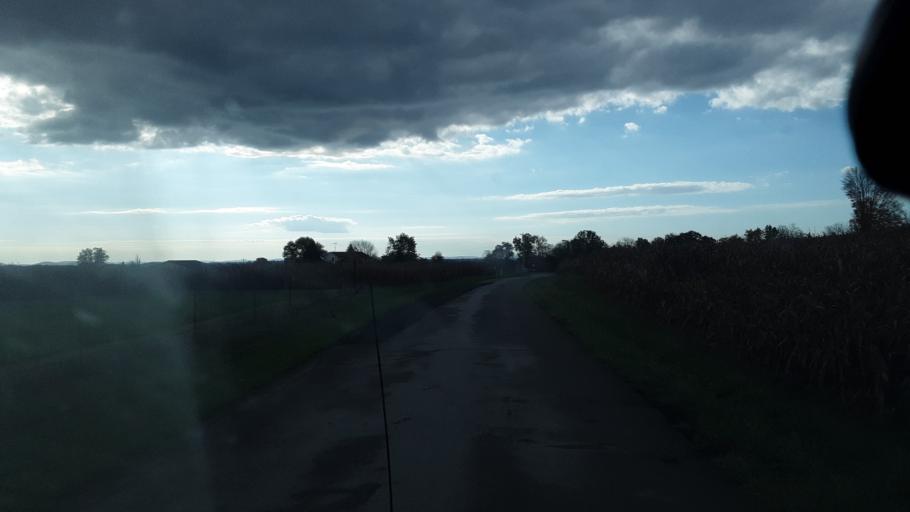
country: US
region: Ohio
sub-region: Highland County
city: Leesburg
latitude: 39.3599
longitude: -83.4793
